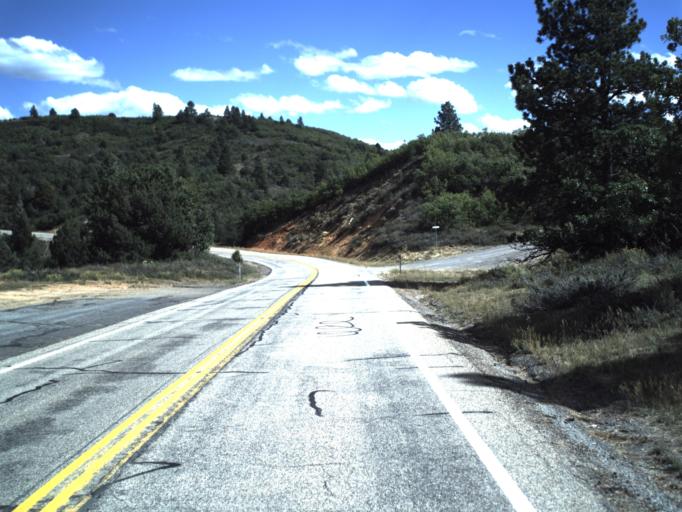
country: US
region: Utah
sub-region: Garfield County
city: Panguitch
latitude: 37.4963
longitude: -112.5429
